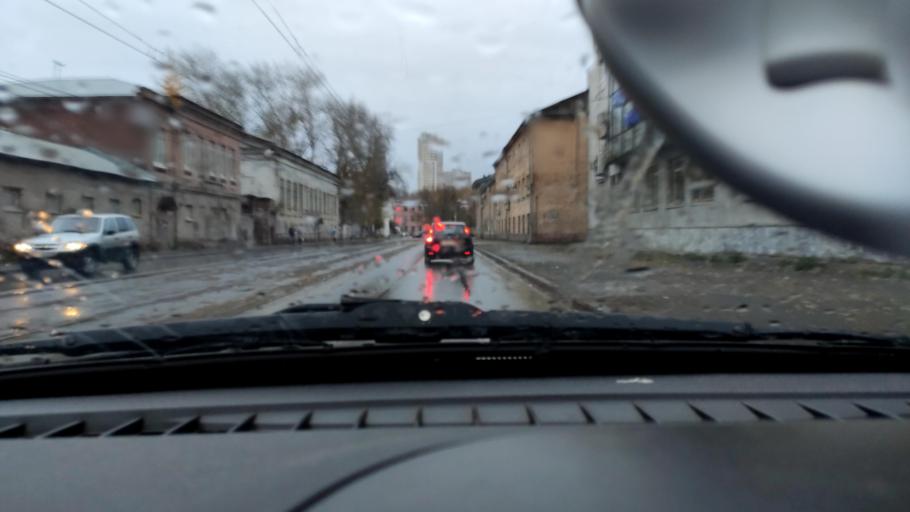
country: RU
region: Perm
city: Perm
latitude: 58.0093
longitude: 56.1882
